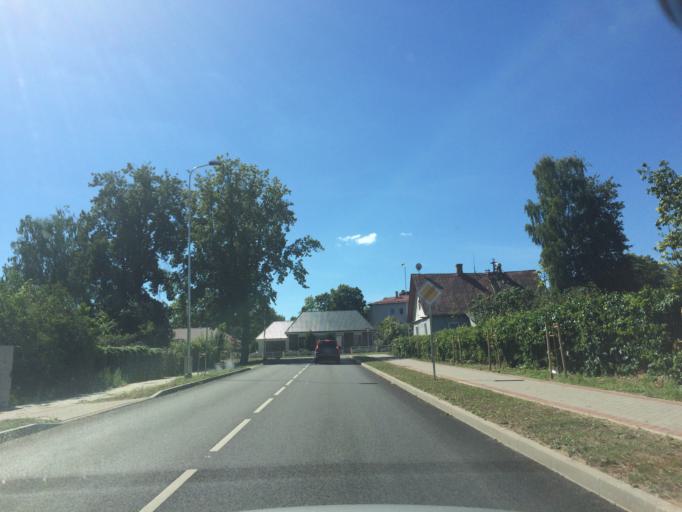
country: LV
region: Rezekne
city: Rezekne
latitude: 56.5065
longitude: 27.3401
